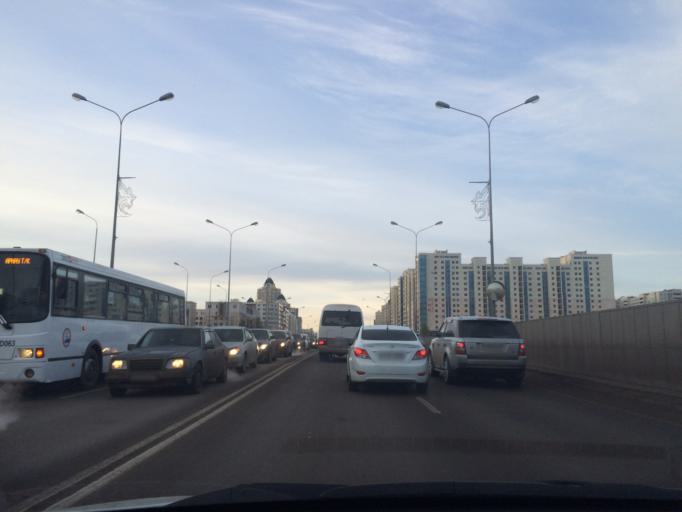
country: KZ
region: Astana Qalasy
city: Astana
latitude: 51.1202
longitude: 71.4358
